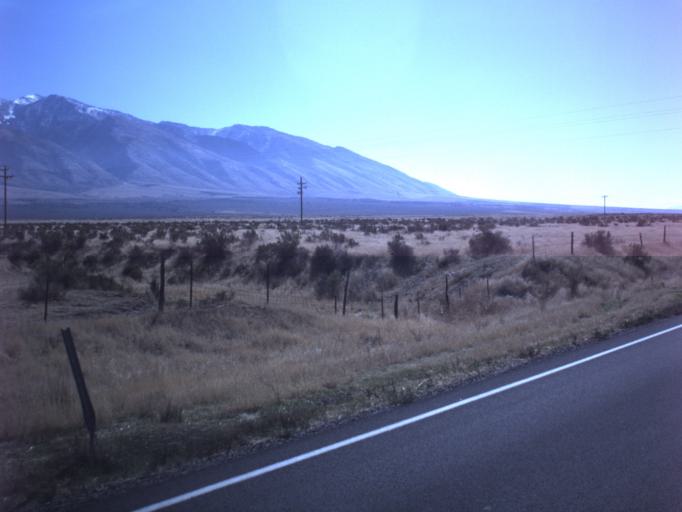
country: US
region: Utah
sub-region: Tooele County
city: Grantsville
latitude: 40.5236
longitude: -112.7477
